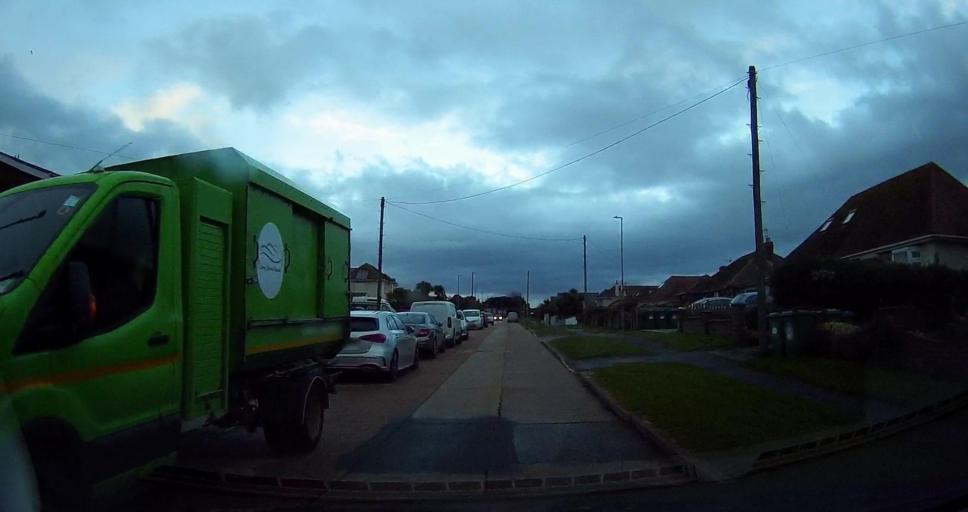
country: GB
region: England
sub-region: East Sussex
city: Peacehaven
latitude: 50.7948
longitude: -0.0116
